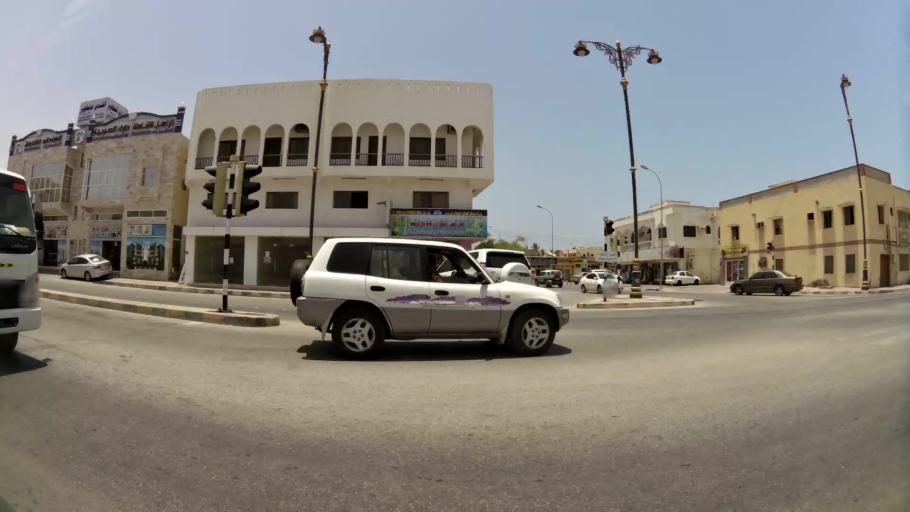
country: OM
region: Zufar
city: Salalah
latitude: 17.0152
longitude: 54.1095
